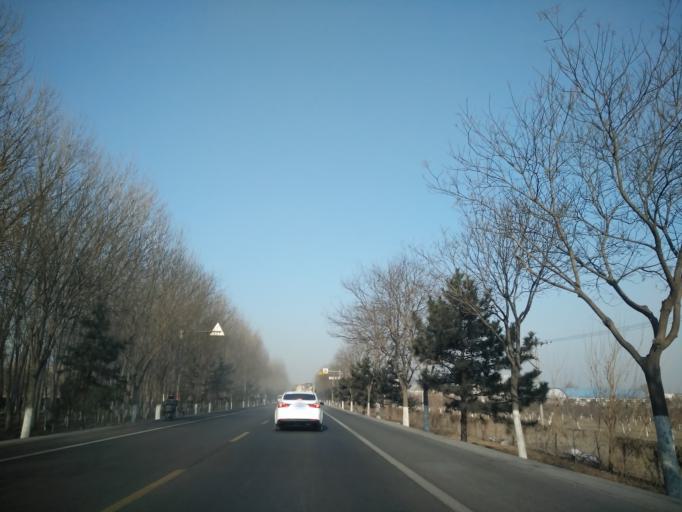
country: CN
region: Beijing
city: Qingyundian
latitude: 39.6663
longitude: 116.5456
